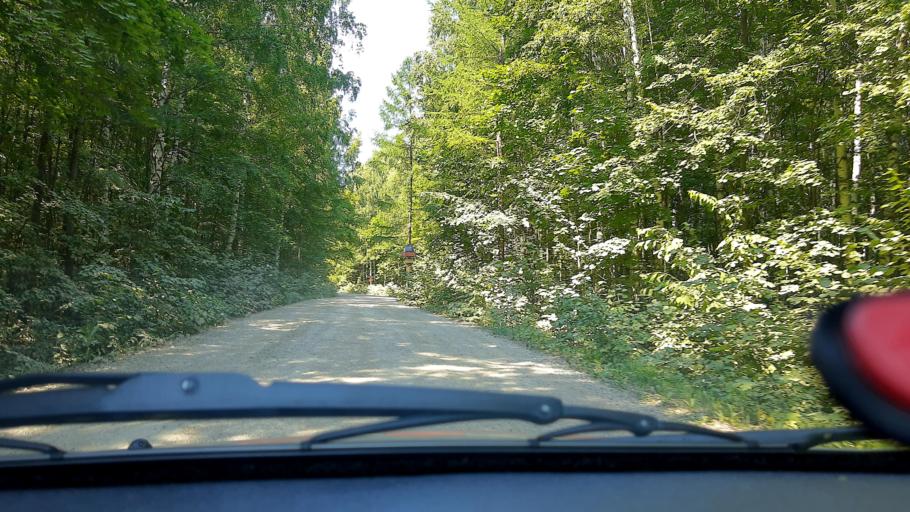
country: RU
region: Bashkortostan
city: Karmaskaly
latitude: 54.3849
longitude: 55.9137
